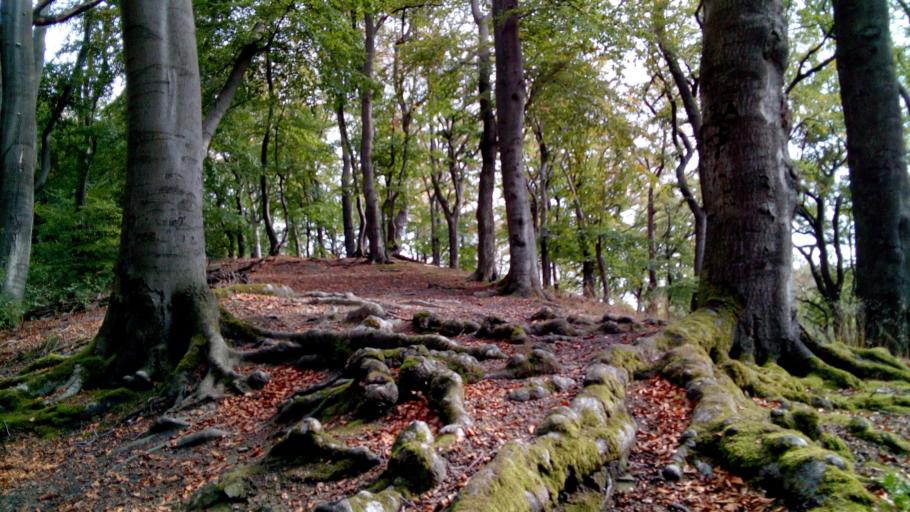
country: DE
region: North Rhine-Westphalia
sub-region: Regierungsbezirk Arnsberg
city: Bochum
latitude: 51.4403
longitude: 7.2534
